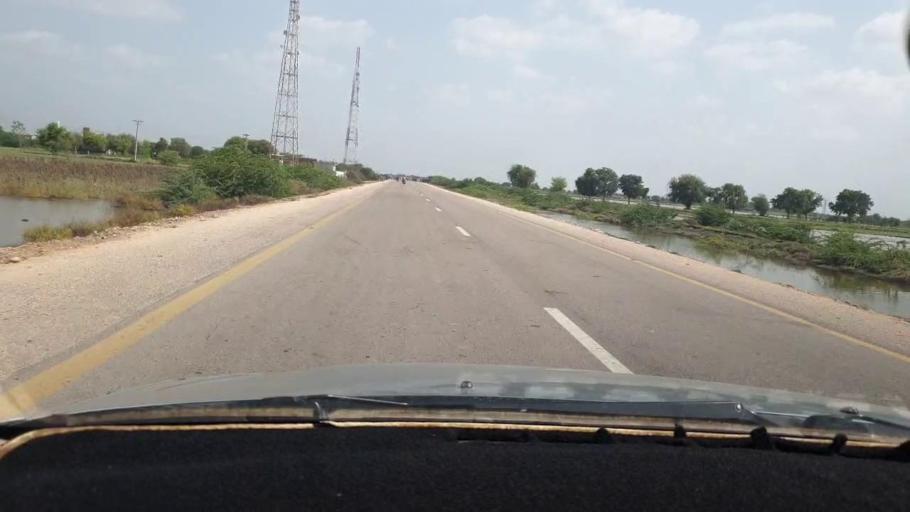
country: PK
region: Sindh
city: Digri
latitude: 25.0281
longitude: 69.2484
